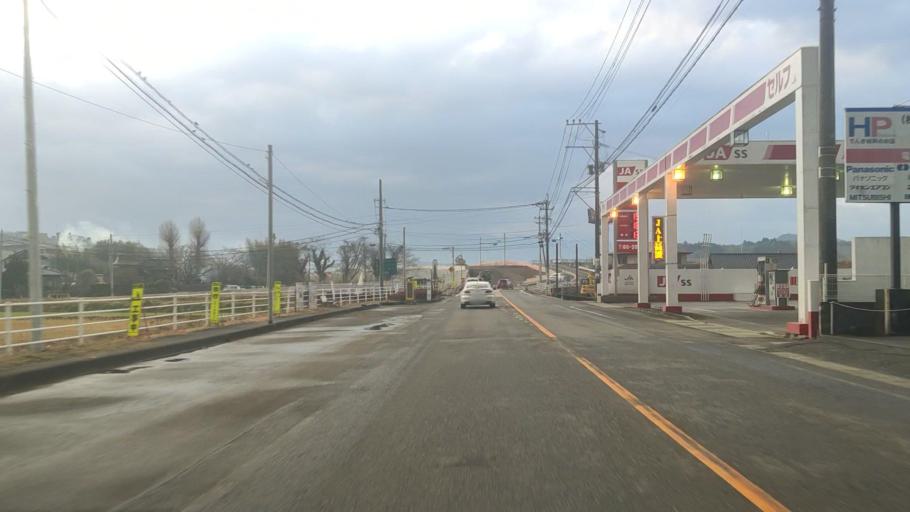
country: JP
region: Kumamoto
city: Uto
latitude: 32.7038
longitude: 130.7784
